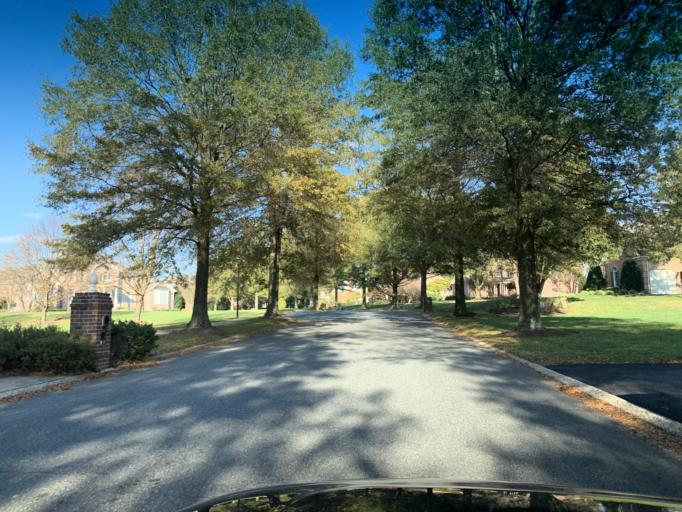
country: US
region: Maryland
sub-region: Harford County
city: Bel Air South
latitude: 39.5159
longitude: -76.3059
